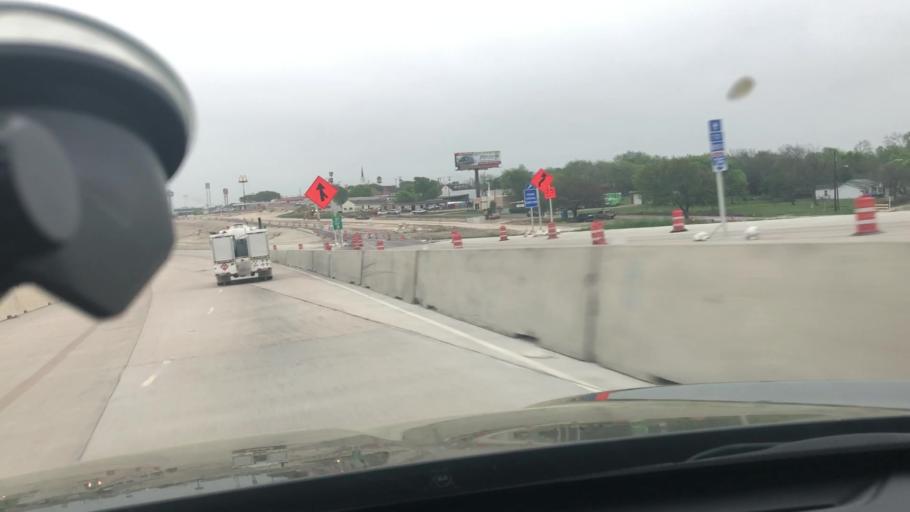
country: US
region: Texas
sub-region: Bell County
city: Temple
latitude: 31.0990
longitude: -97.3628
